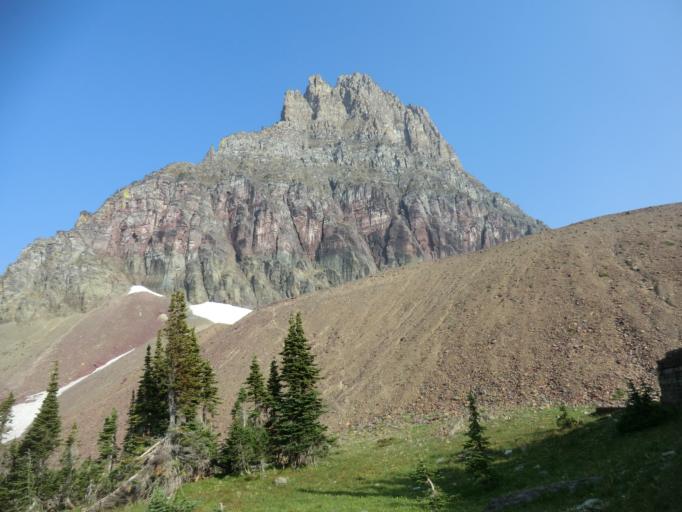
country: US
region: Montana
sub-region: Flathead County
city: Columbia Falls
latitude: 48.6886
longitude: -113.7357
